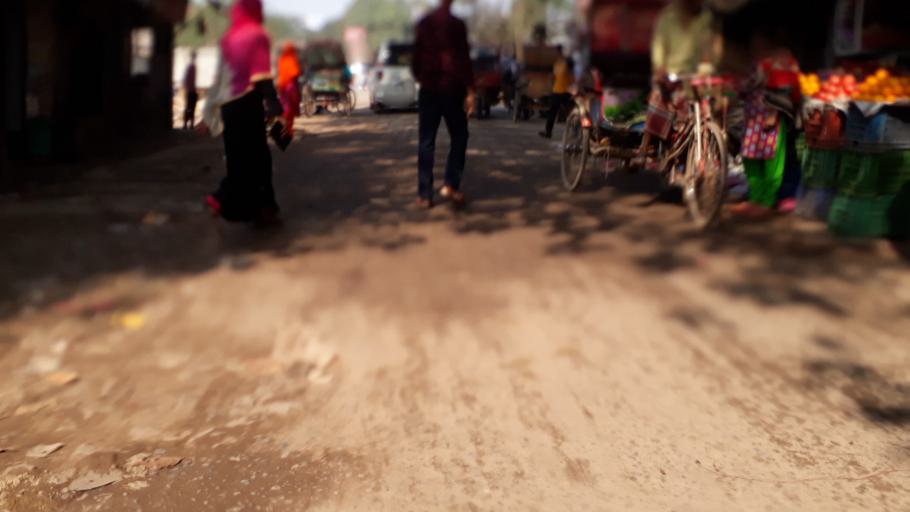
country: BD
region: Dhaka
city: Tungi
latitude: 23.8963
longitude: 90.3319
